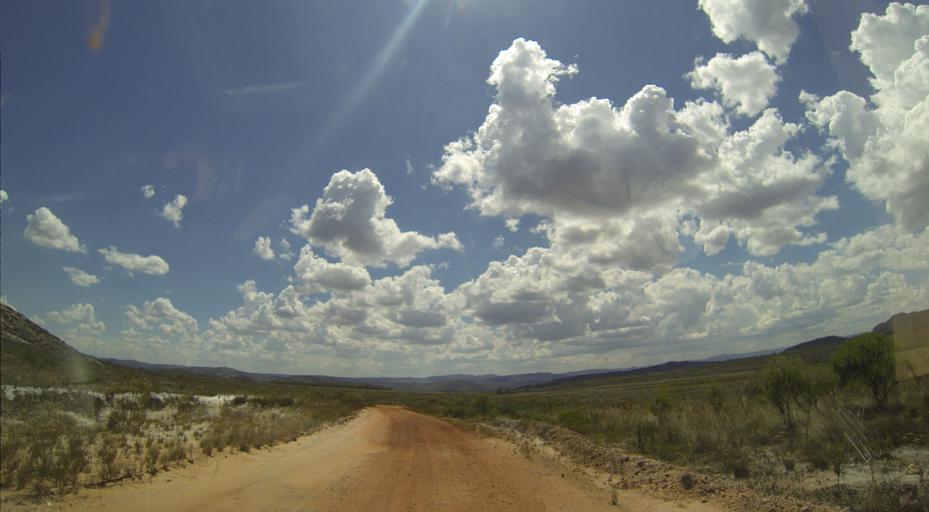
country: BR
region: Minas Gerais
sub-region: Serro
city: Serro
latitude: -18.4763
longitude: -43.4599
